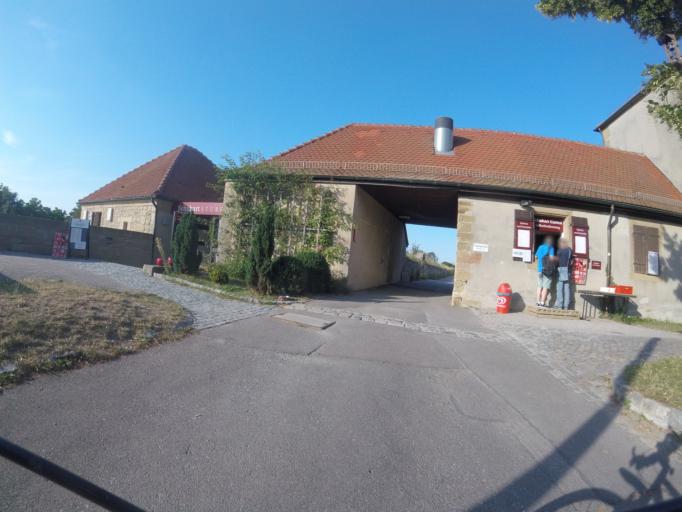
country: DE
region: Baden-Wuerttemberg
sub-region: Regierungsbezirk Stuttgart
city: Asperg
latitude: 48.9105
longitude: 9.1373
